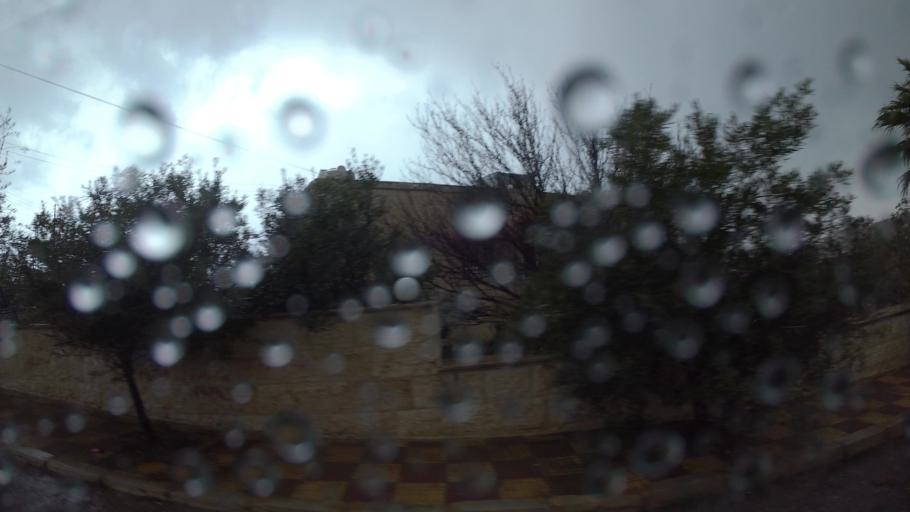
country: JO
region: Amman
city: Umm as Summaq
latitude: 31.8728
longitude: 35.8636
